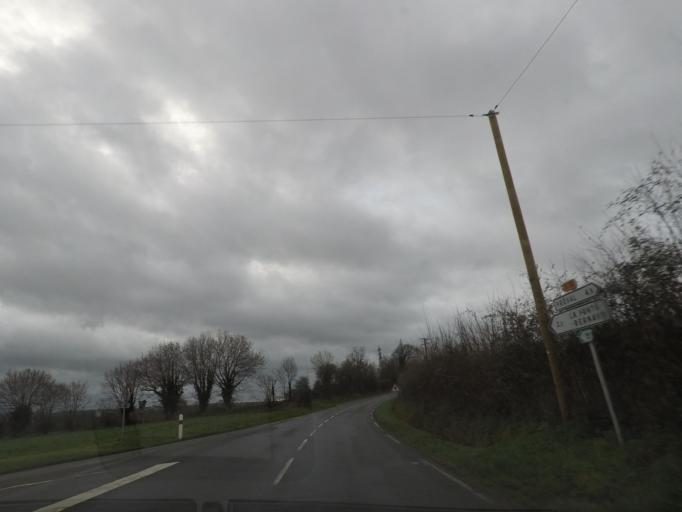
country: FR
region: Pays de la Loire
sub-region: Departement de la Sarthe
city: La Ferte-Bernard
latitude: 48.2017
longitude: 0.6372
